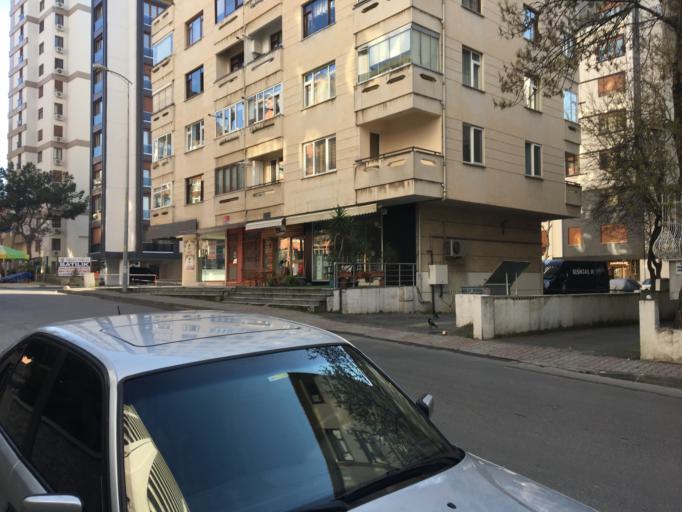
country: TR
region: Istanbul
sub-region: Atasehir
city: Atasehir
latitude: 40.9601
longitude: 29.0972
